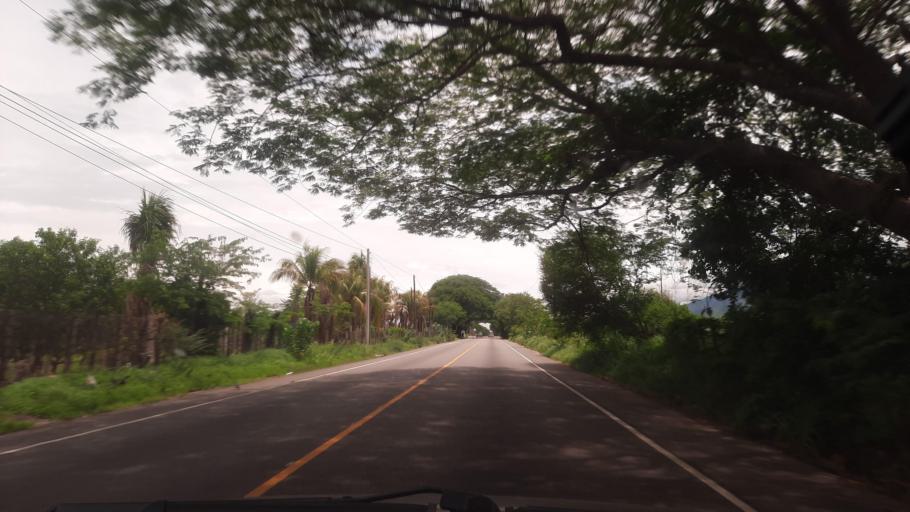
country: GT
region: Zacapa
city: Rio Hondo
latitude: 15.0595
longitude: -89.5428
